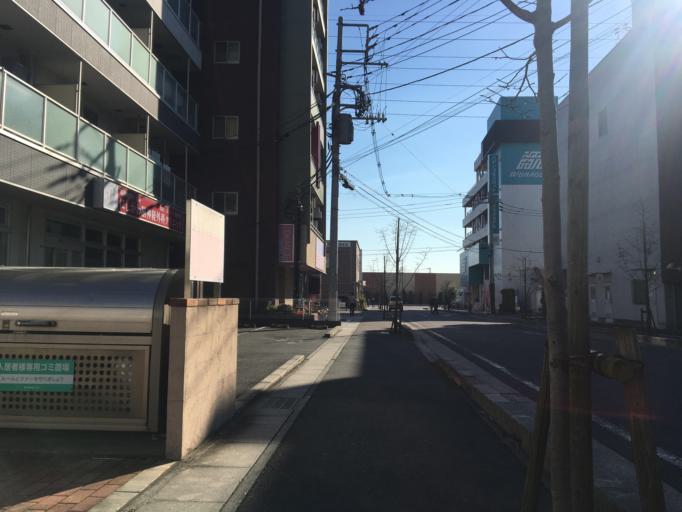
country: JP
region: Saitama
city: Yashio-shi
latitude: 35.8073
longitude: 139.8451
